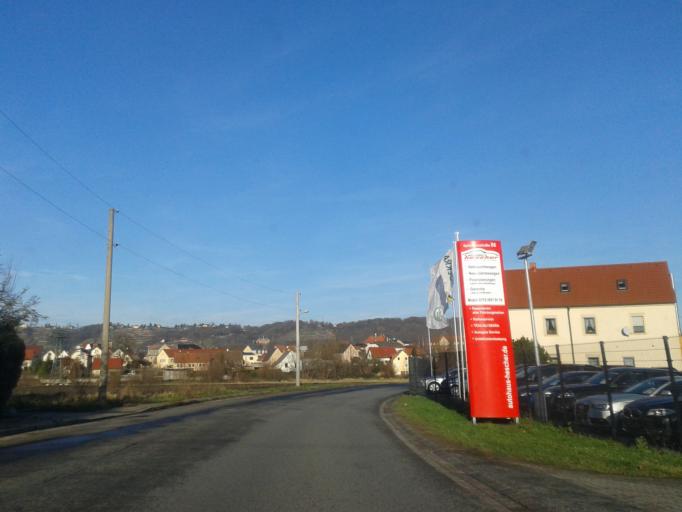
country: DE
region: Saxony
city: Radebeul
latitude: 51.0938
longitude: 13.6744
